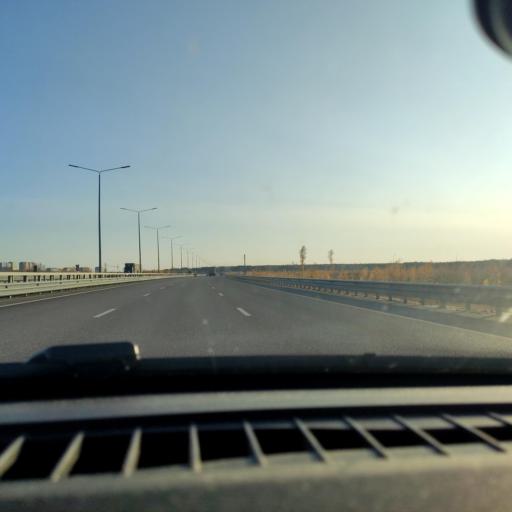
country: RU
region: Voronezj
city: Somovo
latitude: 51.7583
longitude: 39.3071
